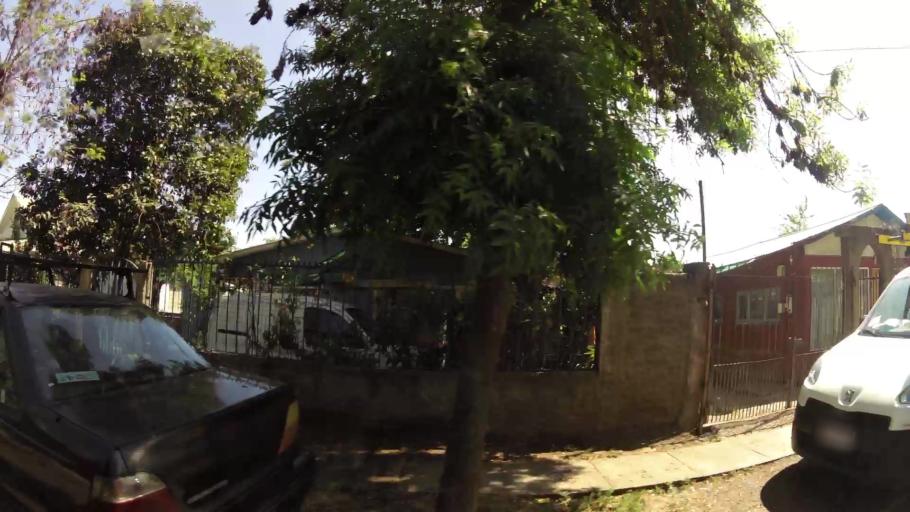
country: CL
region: Santiago Metropolitan
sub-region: Provincia de Santiago
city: Villa Presidente Frei, Nunoa, Santiago, Chile
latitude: -33.4648
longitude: -70.5377
